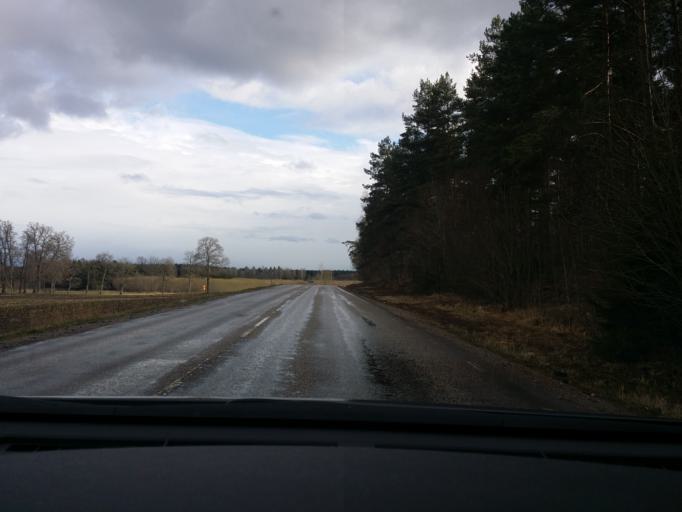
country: SE
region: Soedermanland
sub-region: Eskilstuna Kommun
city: Arla
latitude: 59.3089
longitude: 16.6829
